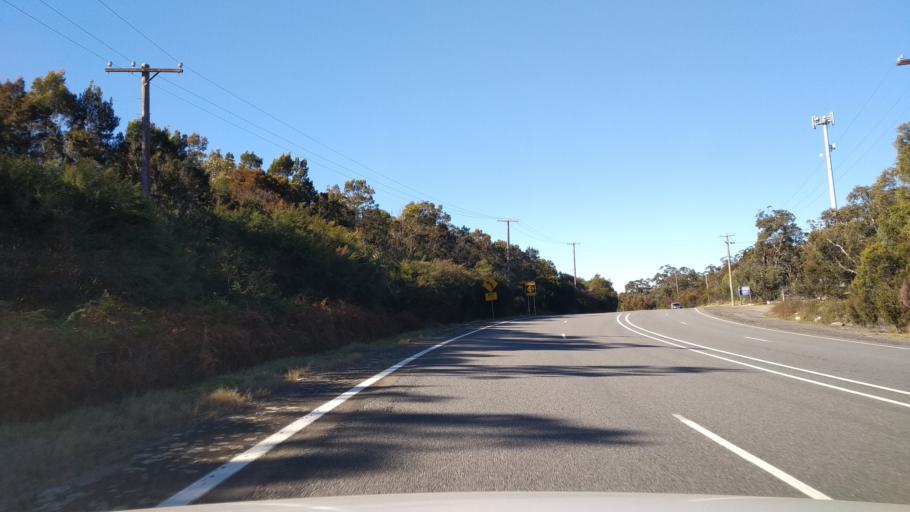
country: AU
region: New South Wales
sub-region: Gosford Shire
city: Point Clare
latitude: -33.3950
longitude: 151.2173
